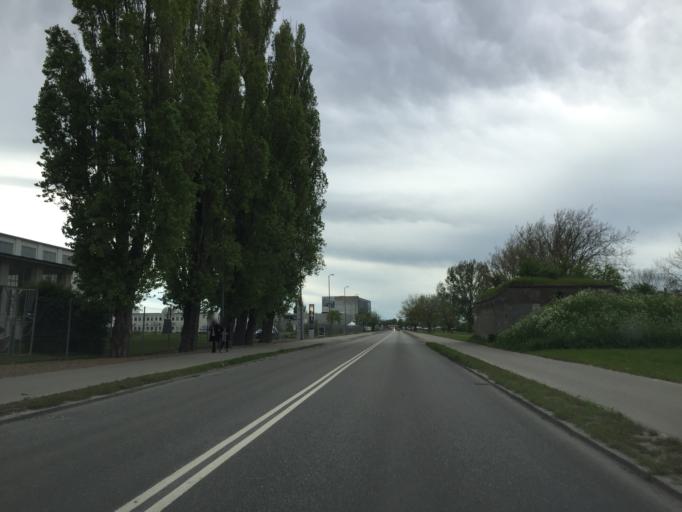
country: DK
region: Capital Region
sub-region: Kobenhavn
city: Christianshavn
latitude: 55.6660
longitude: 12.6284
